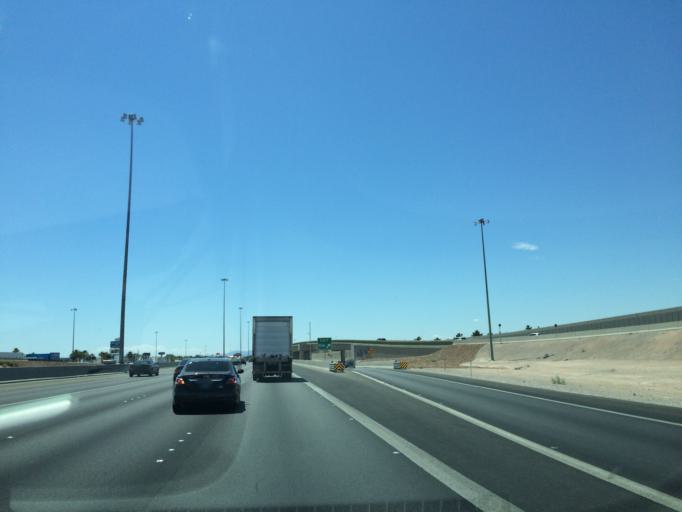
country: US
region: Nevada
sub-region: Clark County
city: Las Vegas
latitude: 36.2626
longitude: -115.2535
